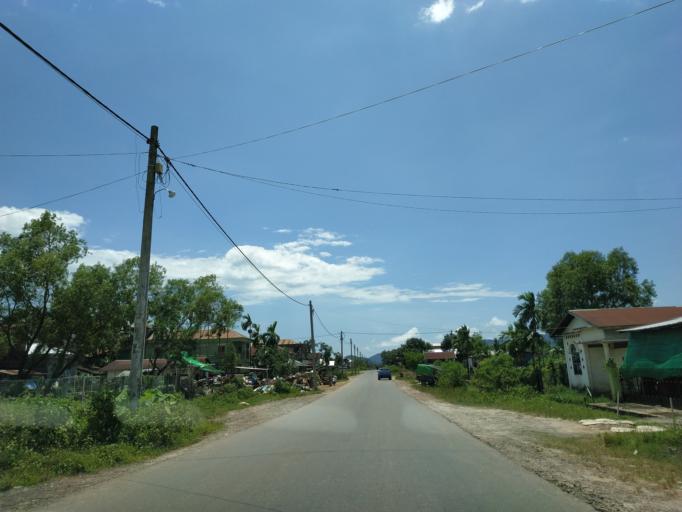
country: MM
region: Tanintharyi
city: Dawei
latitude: 14.0981
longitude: 98.1900
